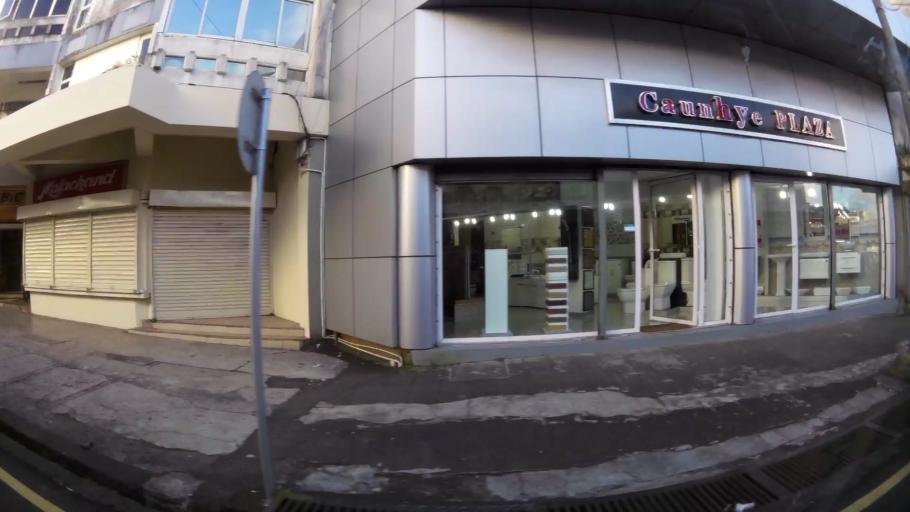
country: MU
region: Plaines Wilhems
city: Curepipe
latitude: -20.3151
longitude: 57.5231
